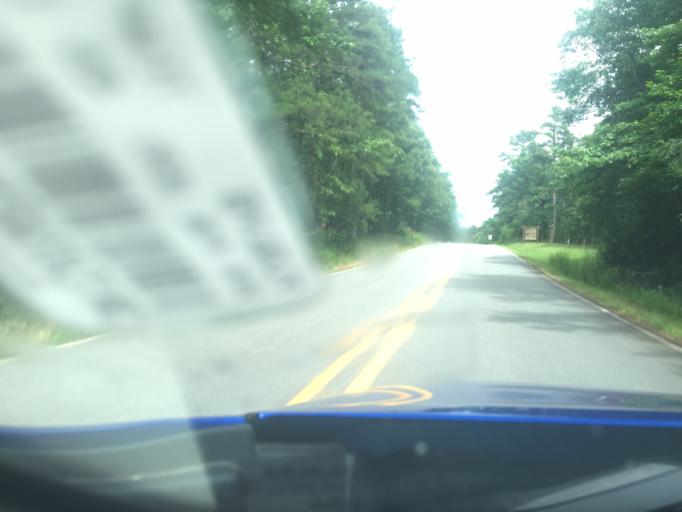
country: US
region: Arkansas
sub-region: Pulaski County
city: Maumelle
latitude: 34.8360
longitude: -92.4696
